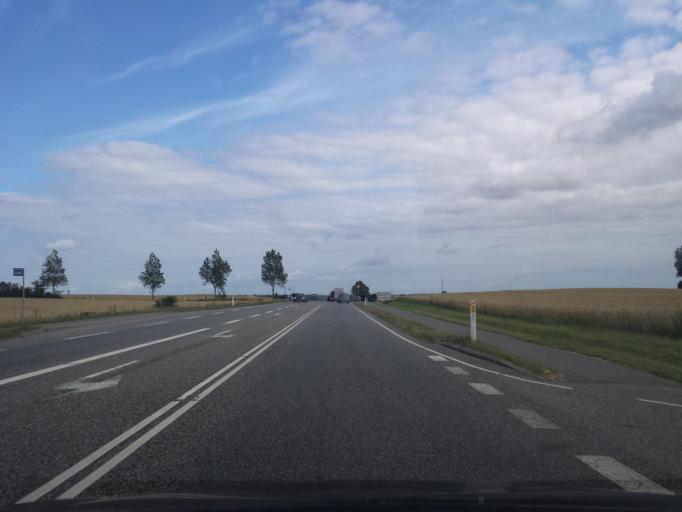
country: DK
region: South Denmark
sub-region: Sonderborg Kommune
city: Guderup
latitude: 54.9846
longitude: 9.8705
